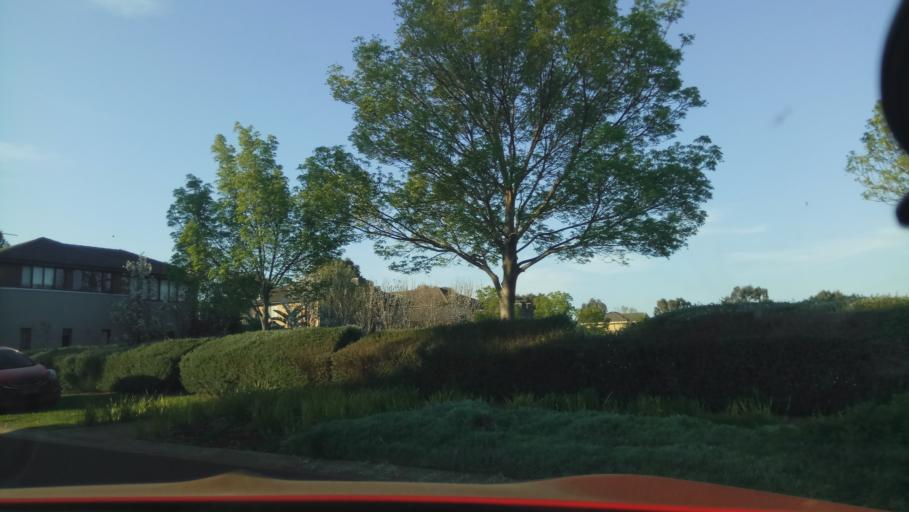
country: AU
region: Victoria
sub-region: Hobsons Bay
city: Altona Meadows
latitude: -37.8906
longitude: 144.7684
